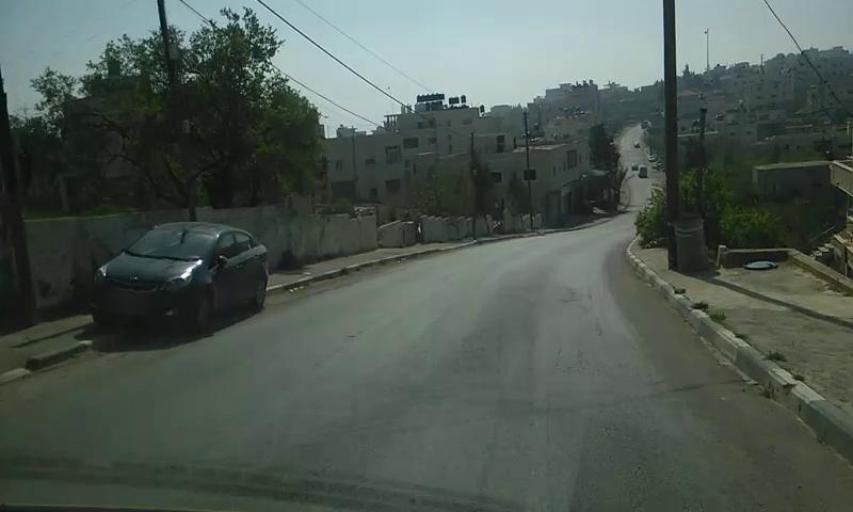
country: PS
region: West Bank
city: Dayr Jarir
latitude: 31.9618
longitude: 35.2955
